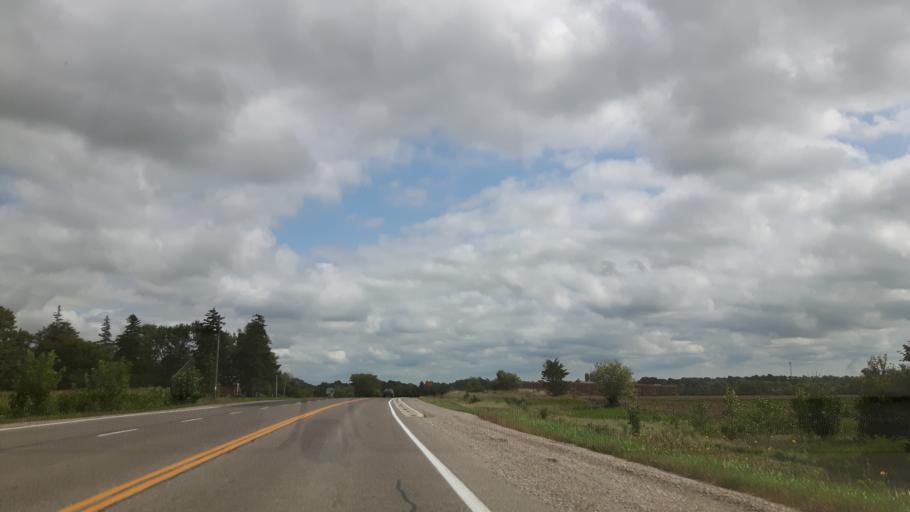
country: CA
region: Ontario
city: South Huron
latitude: 43.1990
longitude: -81.4376
